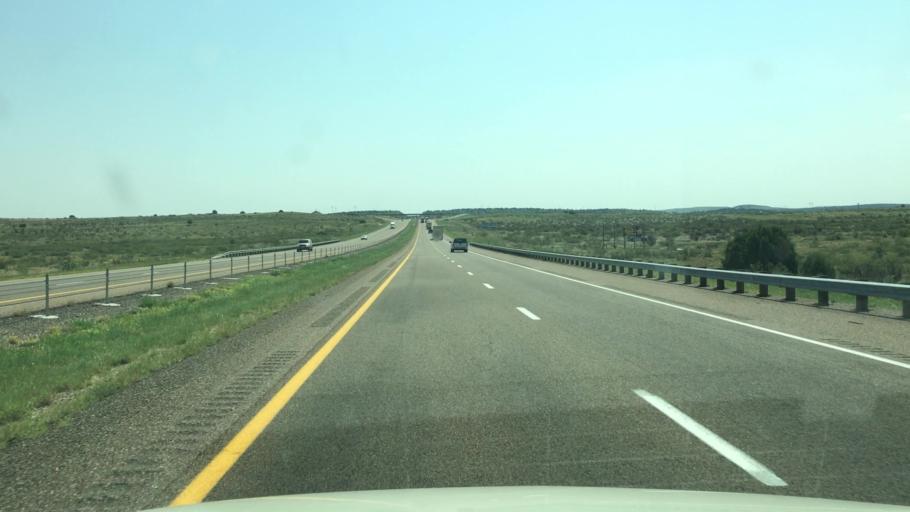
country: US
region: New Mexico
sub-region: Quay County
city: Tucumcari
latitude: 35.1207
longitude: -103.9063
